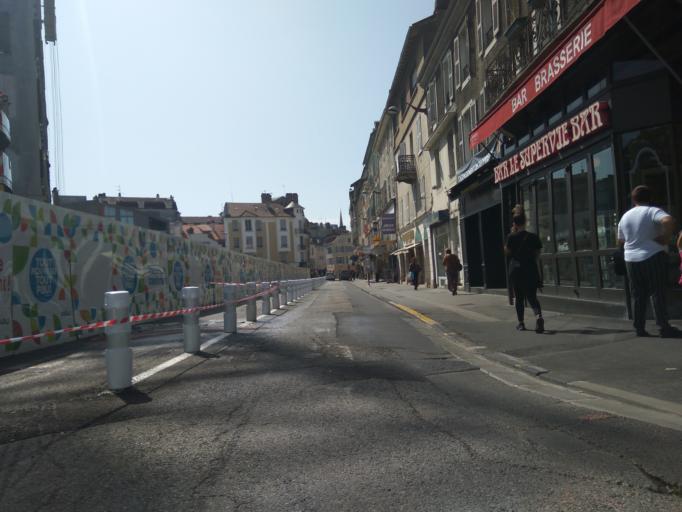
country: FR
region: Aquitaine
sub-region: Departement des Pyrenees-Atlantiques
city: Pau
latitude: 43.2998
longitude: -0.3700
